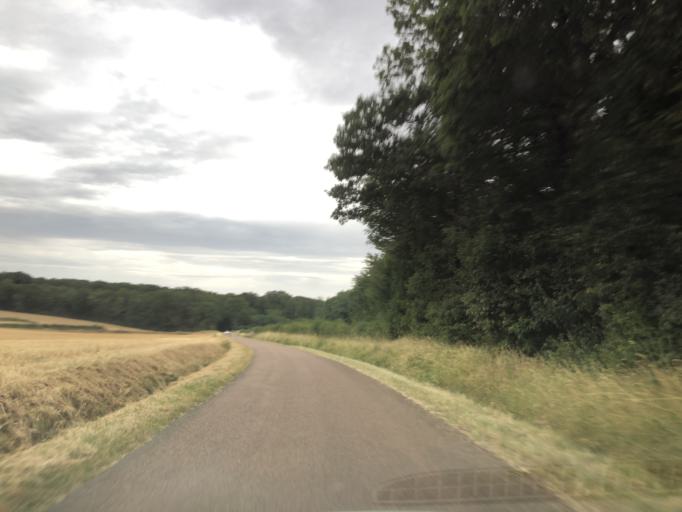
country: FR
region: Bourgogne
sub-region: Departement de l'Yonne
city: Aillant-sur-Tholon
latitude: 47.9030
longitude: 3.3061
